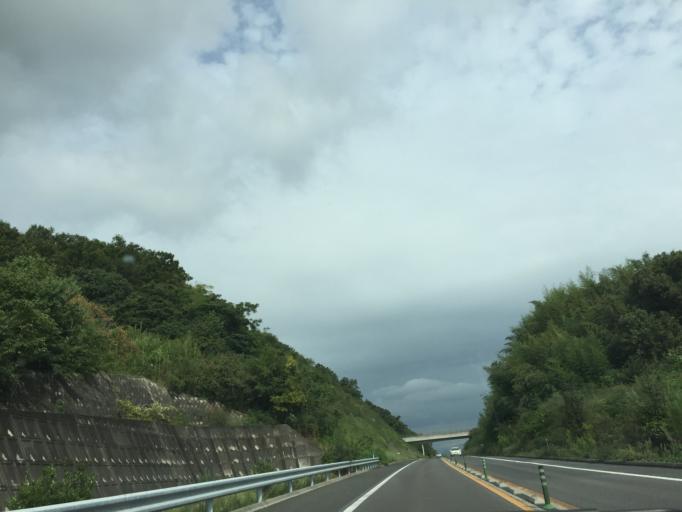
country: JP
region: Kagawa
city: Shido
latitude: 34.2628
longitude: 134.2872
